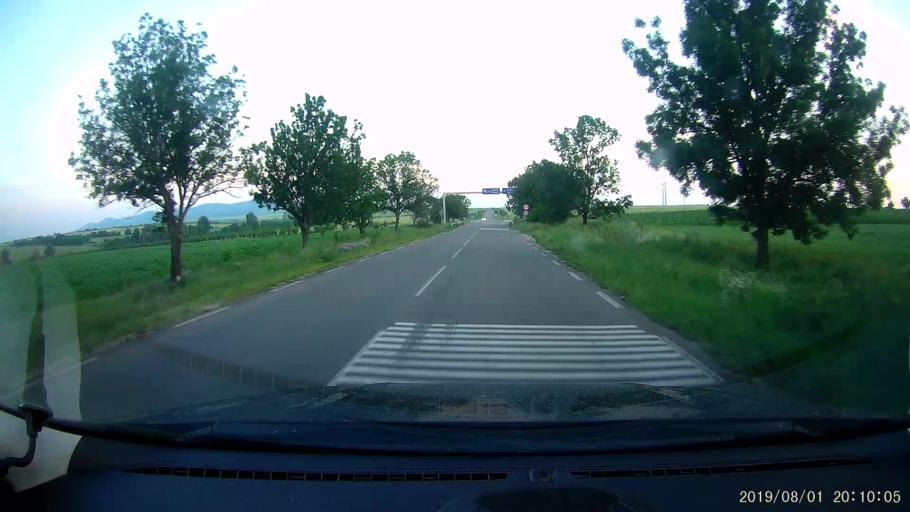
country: BG
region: Yambol
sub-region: Obshtina Yambol
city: Yambol
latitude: 42.4873
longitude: 26.5964
